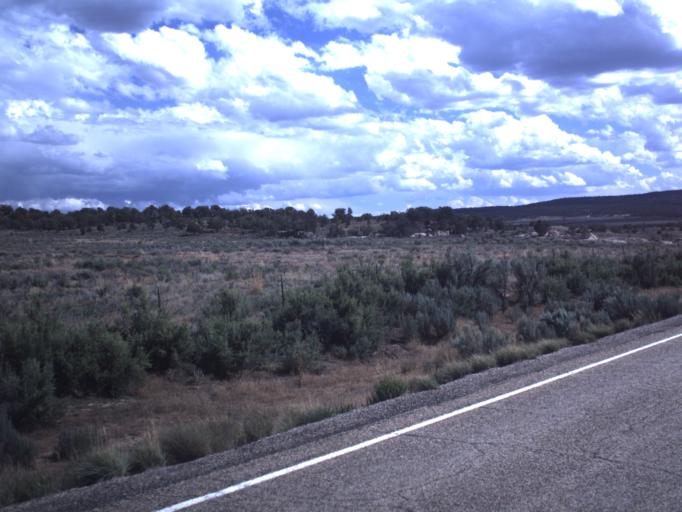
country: US
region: Utah
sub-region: Duchesne County
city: Duchesne
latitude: 40.2309
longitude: -110.7196
